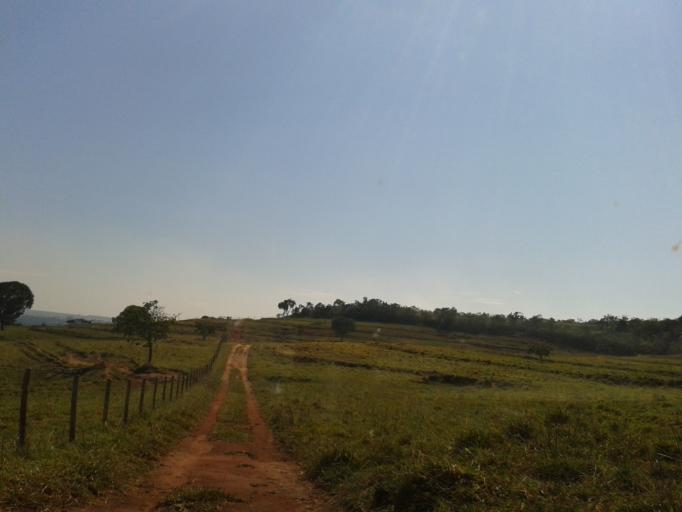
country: BR
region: Minas Gerais
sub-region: Campina Verde
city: Campina Verde
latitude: -19.3836
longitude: -49.6313
